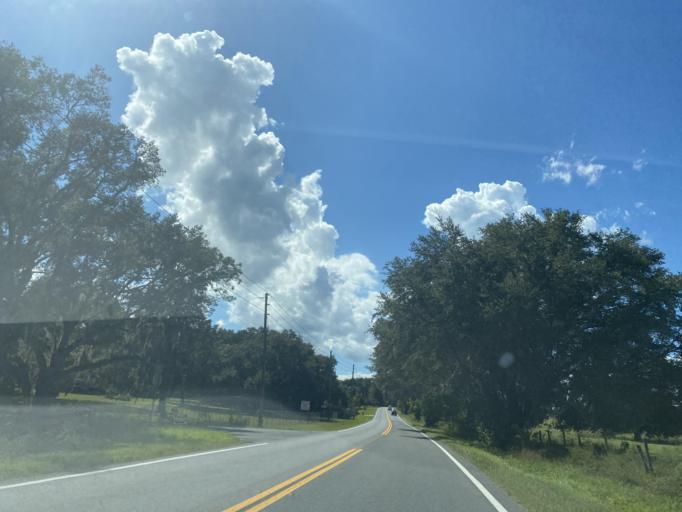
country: US
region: Florida
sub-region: Lake County
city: Lady Lake
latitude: 28.9830
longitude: -81.9057
